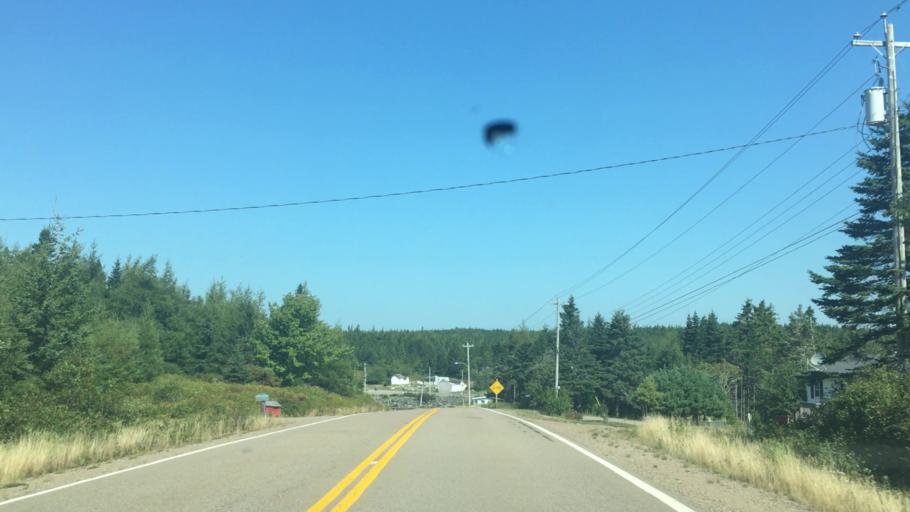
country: CA
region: Nova Scotia
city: Antigonish
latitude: 45.0255
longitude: -62.0311
